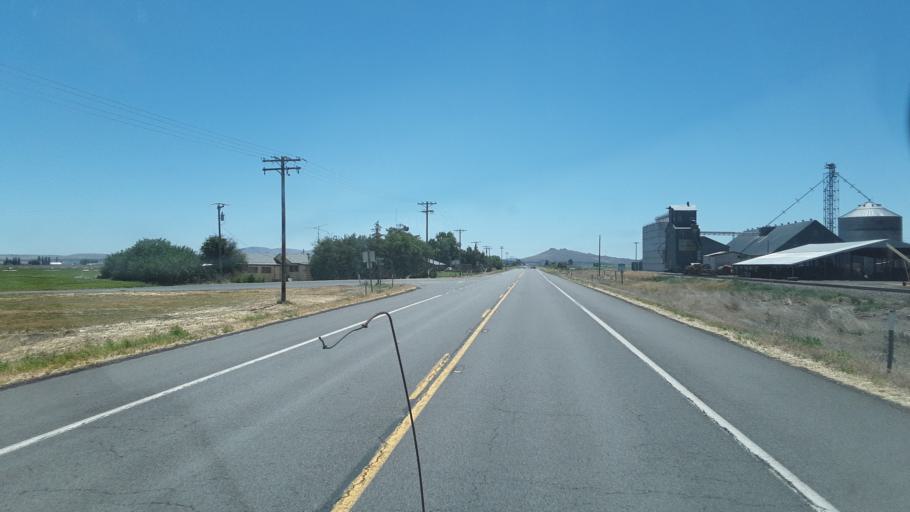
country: US
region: California
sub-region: Siskiyou County
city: Tulelake
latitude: 41.9429
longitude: -121.4581
